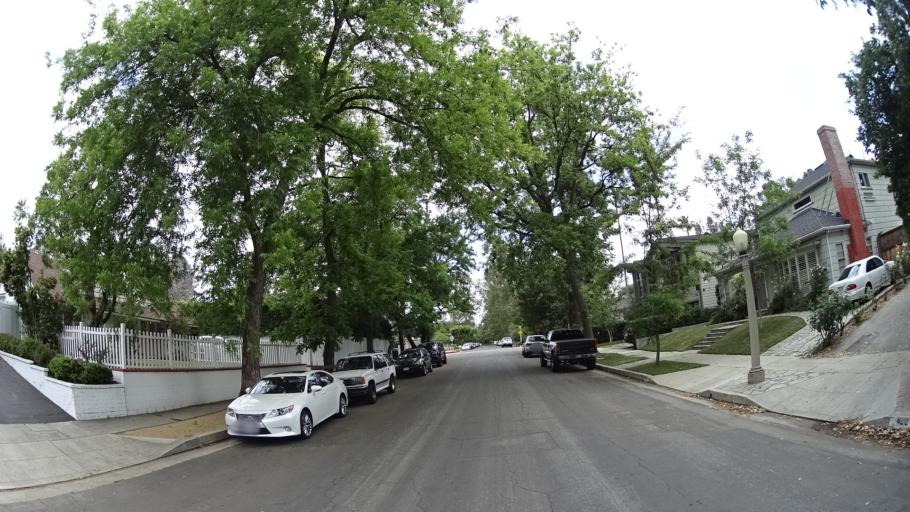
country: US
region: California
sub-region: Los Angeles County
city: North Hollywood
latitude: 34.1480
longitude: -118.3943
